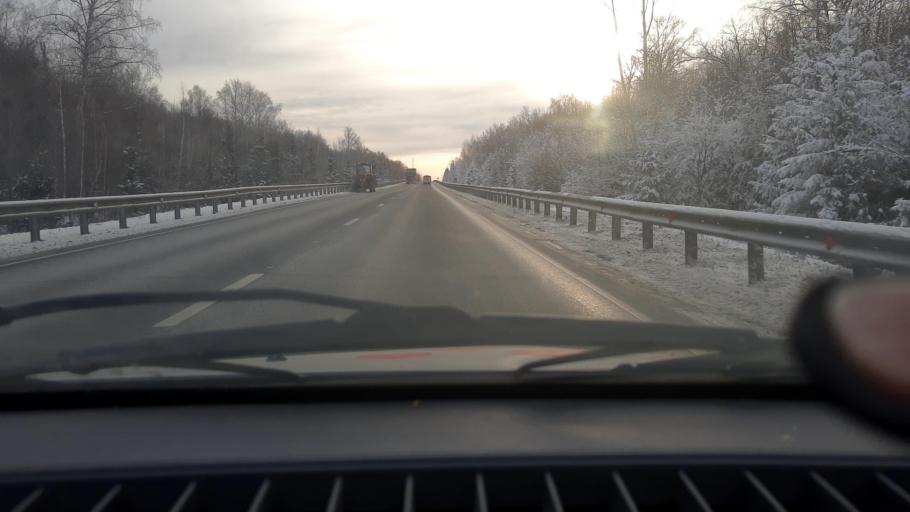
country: RU
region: Bashkortostan
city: Avdon
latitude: 54.8403
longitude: 55.7164
